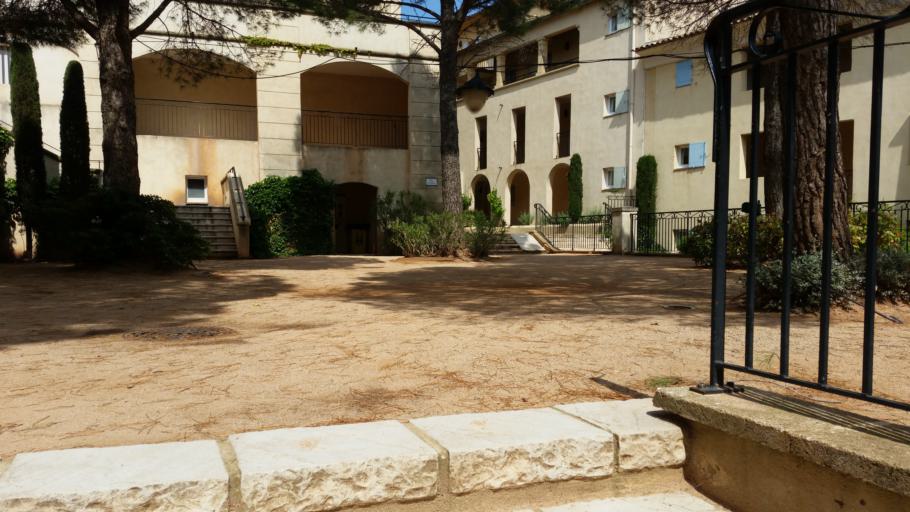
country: FR
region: Provence-Alpes-Cote d'Azur
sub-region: Departement des Bouches-du-Rhone
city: Charleval
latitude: 43.7088
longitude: 5.2113
